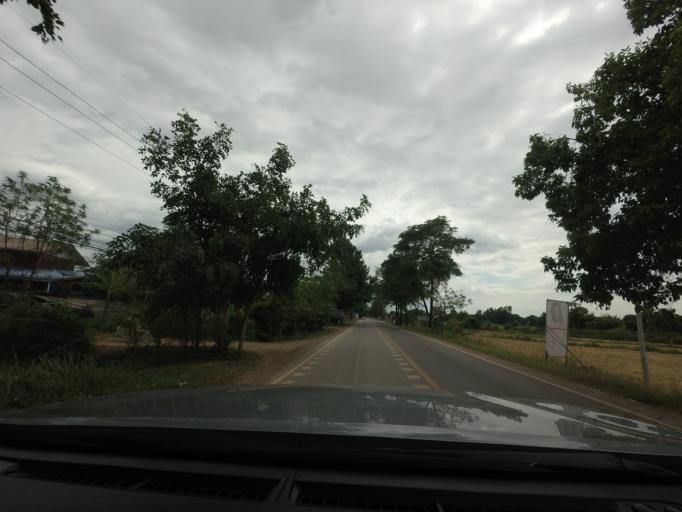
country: TH
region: Phitsanulok
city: Noen Maprang
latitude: 16.6872
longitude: 100.5984
